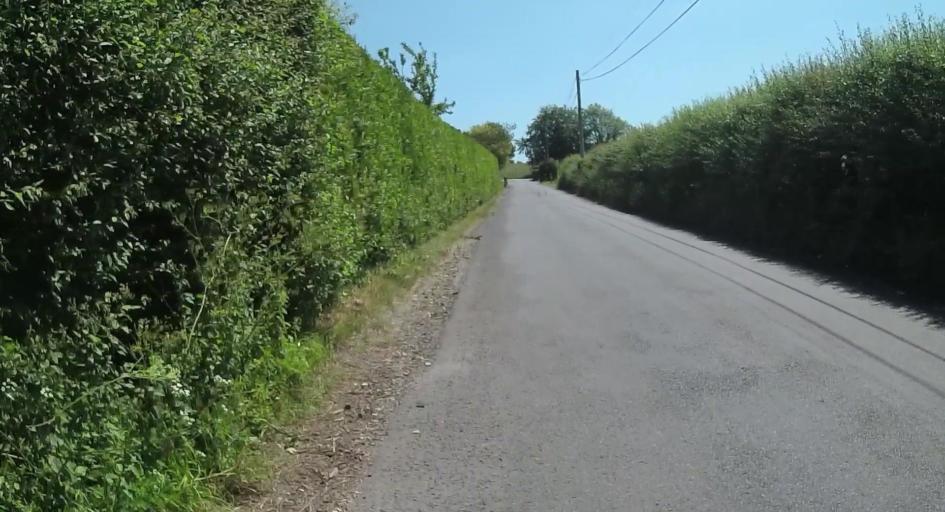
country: GB
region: England
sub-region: Hampshire
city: Kings Worthy
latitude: 51.0632
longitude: -1.2762
